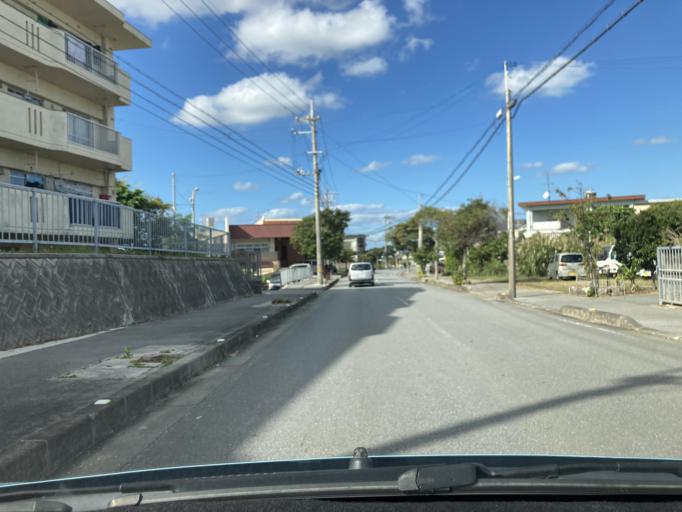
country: JP
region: Okinawa
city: Gushikawa
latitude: 26.3660
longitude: 127.8440
